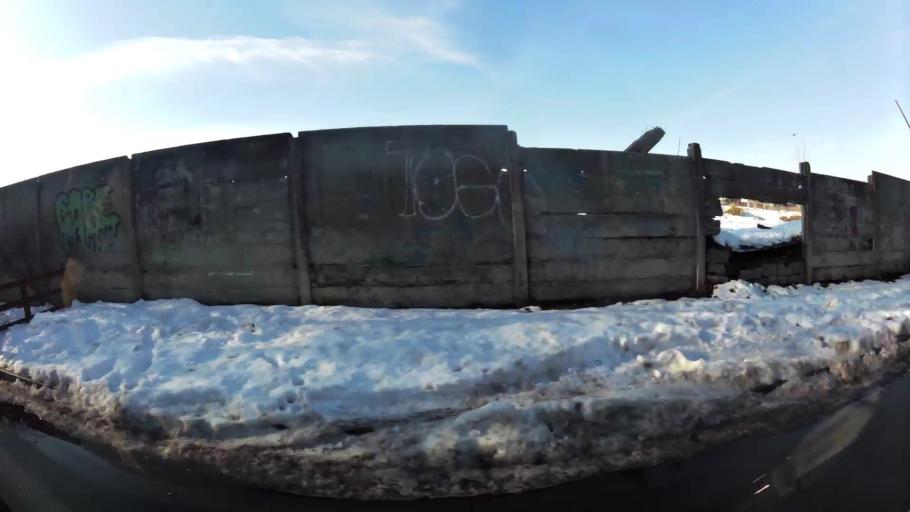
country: RO
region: Bucuresti
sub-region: Municipiul Bucuresti
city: Bucuresti
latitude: 44.3960
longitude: 26.0906
